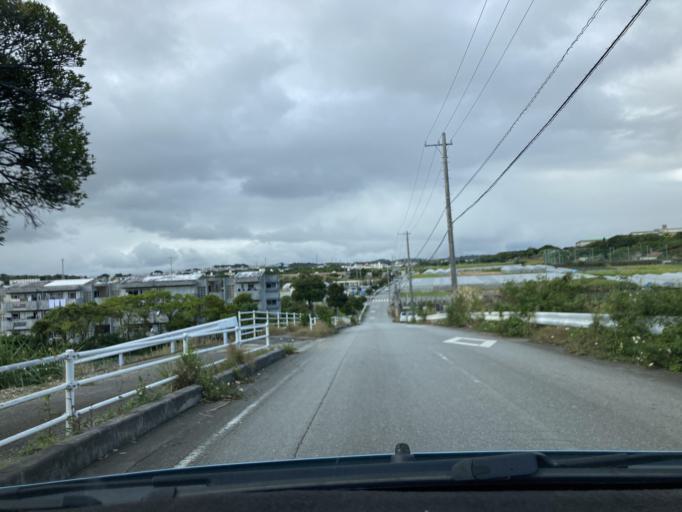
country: JP
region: Okinawa
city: Itoman
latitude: 26.1233
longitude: 127.6867
